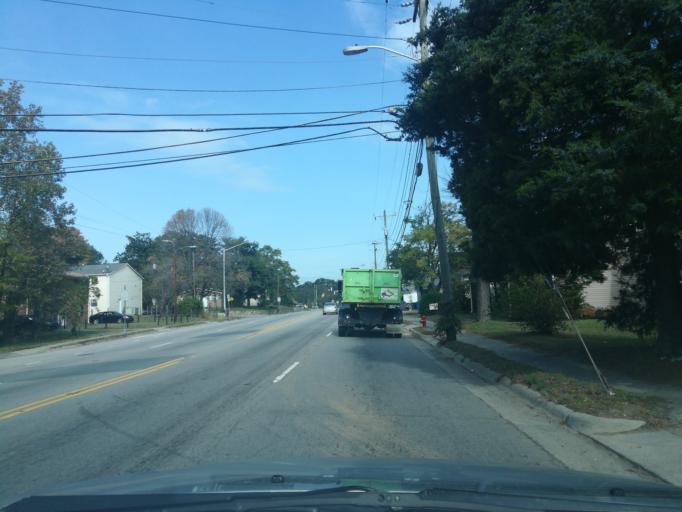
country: US
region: North Carolina
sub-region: Durham County
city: Durham
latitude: 35.9777
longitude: -78.8925
